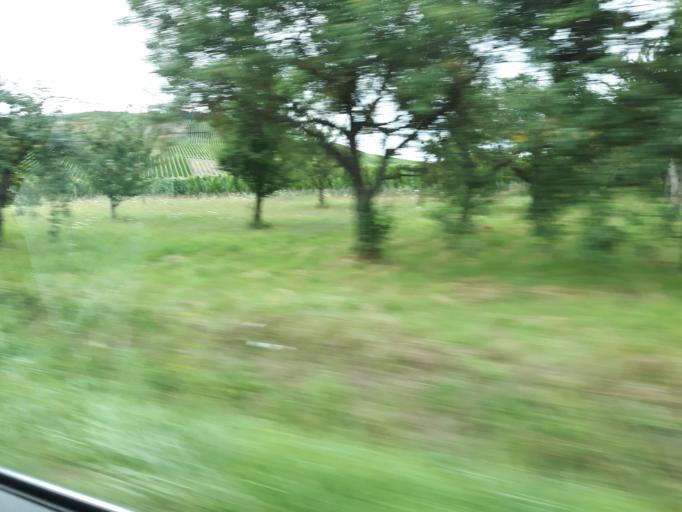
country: DE
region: Baden-Wuerttemberg
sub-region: Regierungsbezirk Stuttgart
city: Weinsberg
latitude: 49.1648
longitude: 9.2847
